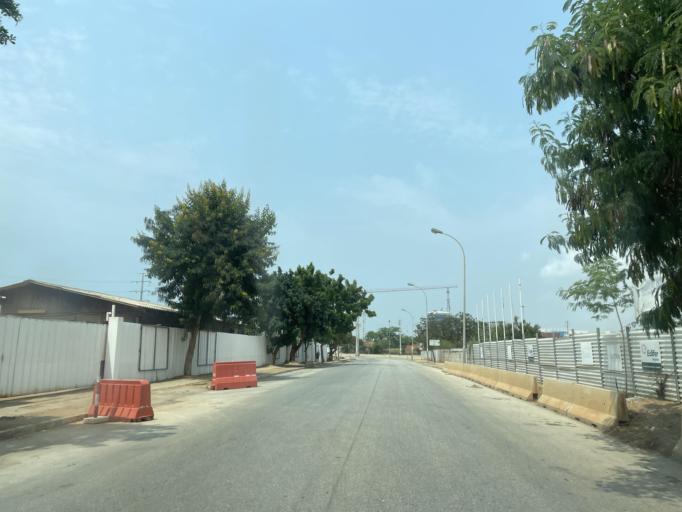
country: AO
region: Luanda
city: Luanda
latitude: -8.9227
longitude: 13.1912
